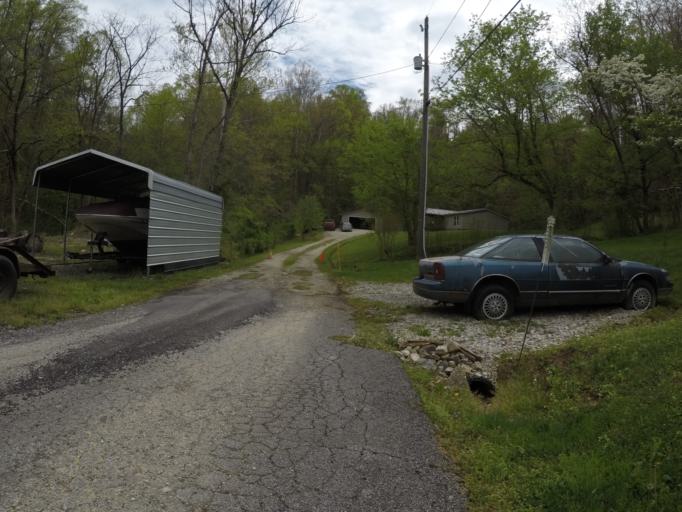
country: US
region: West Virginia
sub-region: Cabell County
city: Huntington
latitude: 38.3886
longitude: -82.4856
